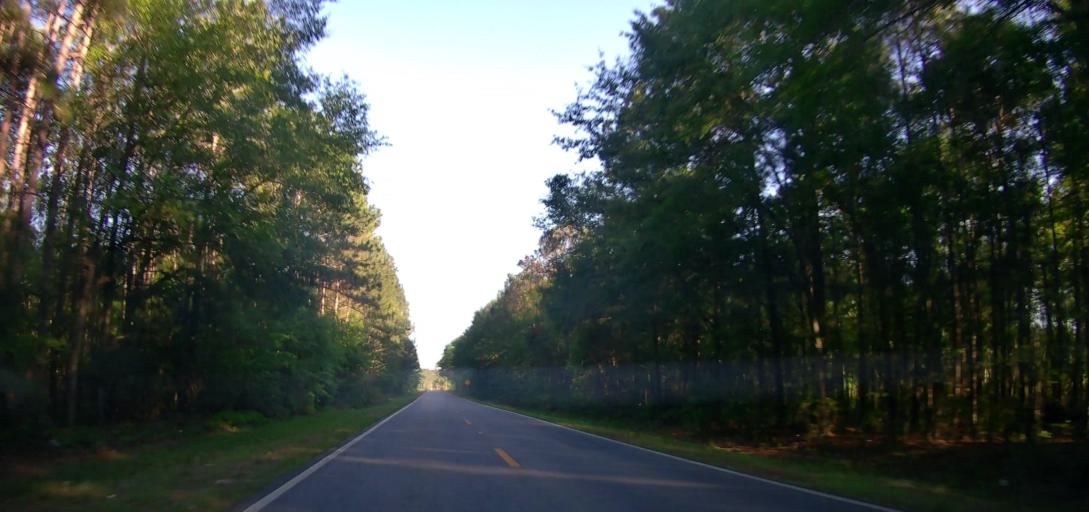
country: US
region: Georgia
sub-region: Ben Hill County
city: Fitzgerald
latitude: 31.6898
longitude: -83.2154
